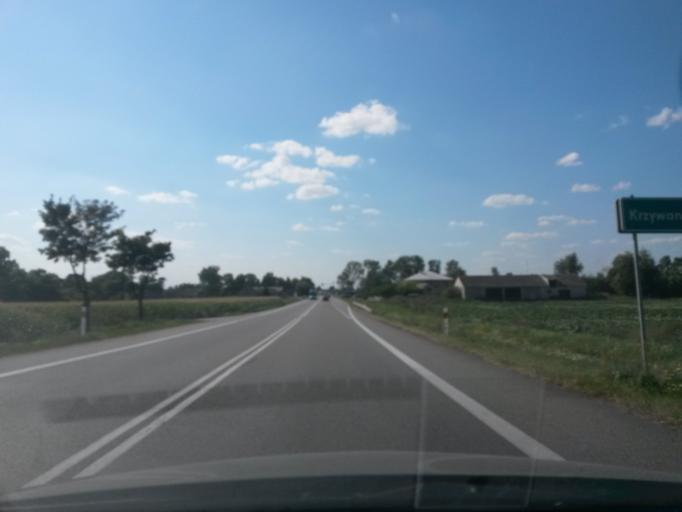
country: PL
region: Masovian Voivodeship
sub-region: Powiat plonski
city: Dzierzaznia
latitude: 52.6379
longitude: 20.1464
